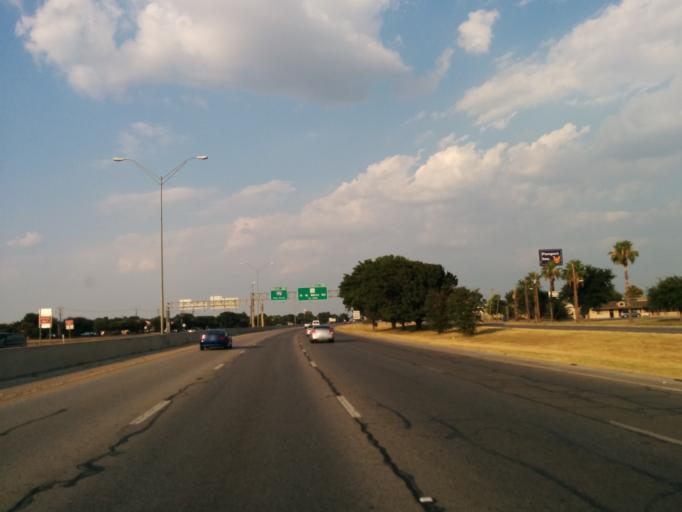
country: US
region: Texas
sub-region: Bexar County
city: Kirby
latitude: 29.4263
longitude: -98.4197
